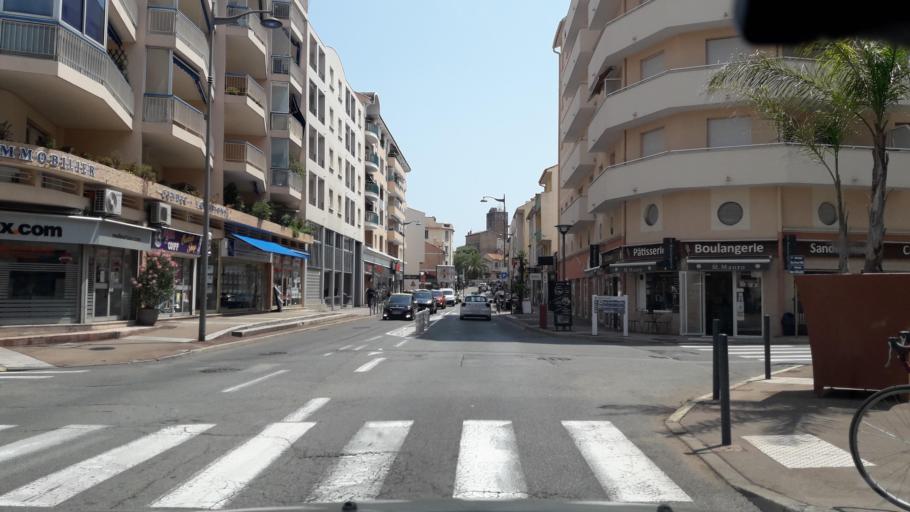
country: FR
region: Provence-Alpes-Cote d'Azur
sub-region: Departement du Var
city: Saint-Raphael
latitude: 43.4274
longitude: 6.7670
